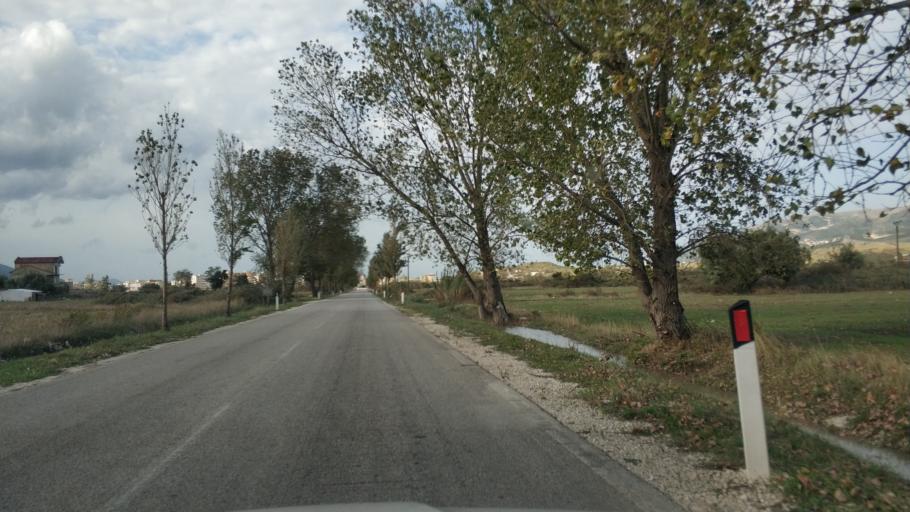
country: AL
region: Vlore
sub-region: Rrethi i Vlores
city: Orikum
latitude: 40.3208
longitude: 19.4820
